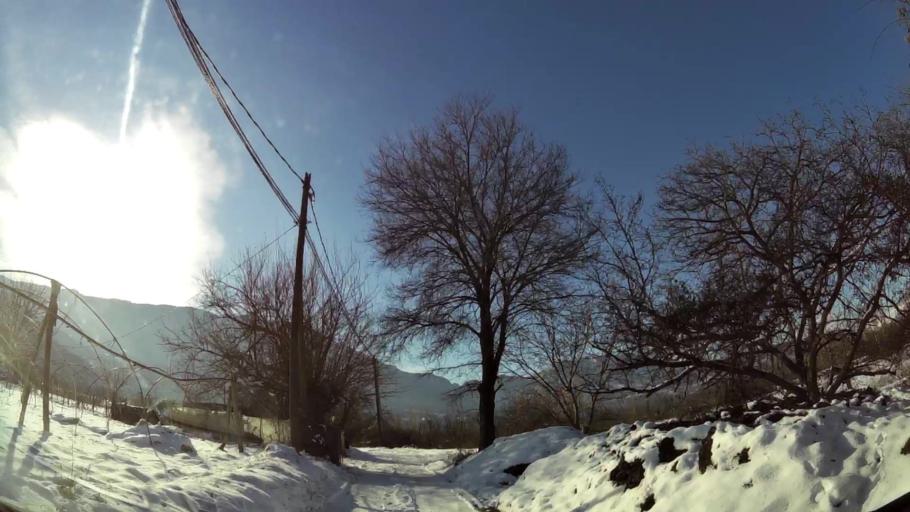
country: MK
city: Grchec
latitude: 41.9862
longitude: 21.3243
